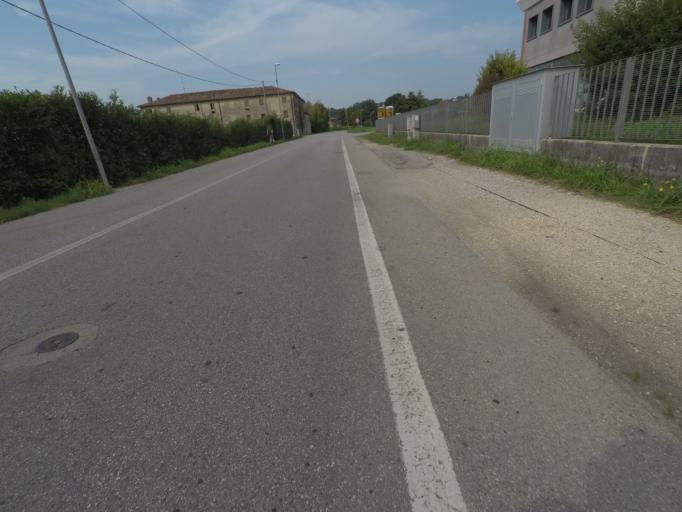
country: IT
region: Veneto
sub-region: Provincia di Treviso
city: Carpesica
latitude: 45.9570
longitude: 12.3061
